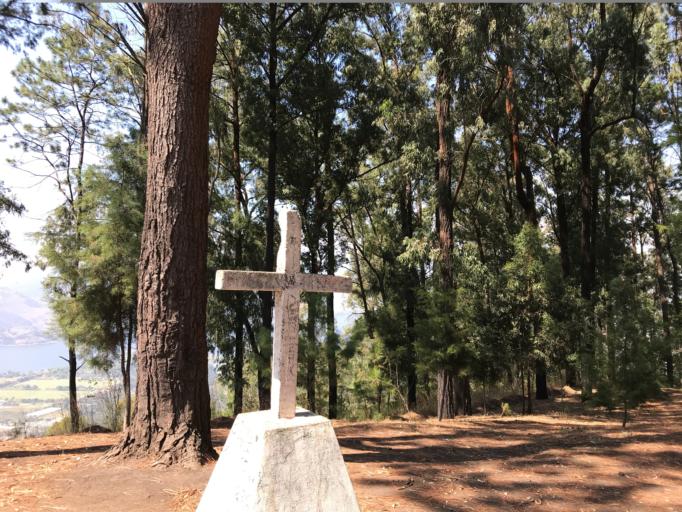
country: GT
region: Guatemala
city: Villa Canales
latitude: 14.4788
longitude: -90.5473
